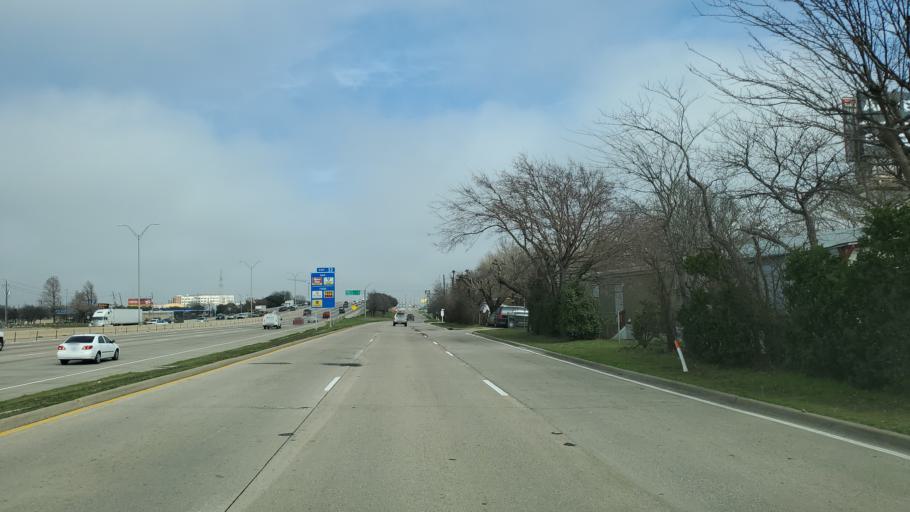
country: US
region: Texas
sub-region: Collin County
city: Plano
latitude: 33.0525
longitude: -96.6961
